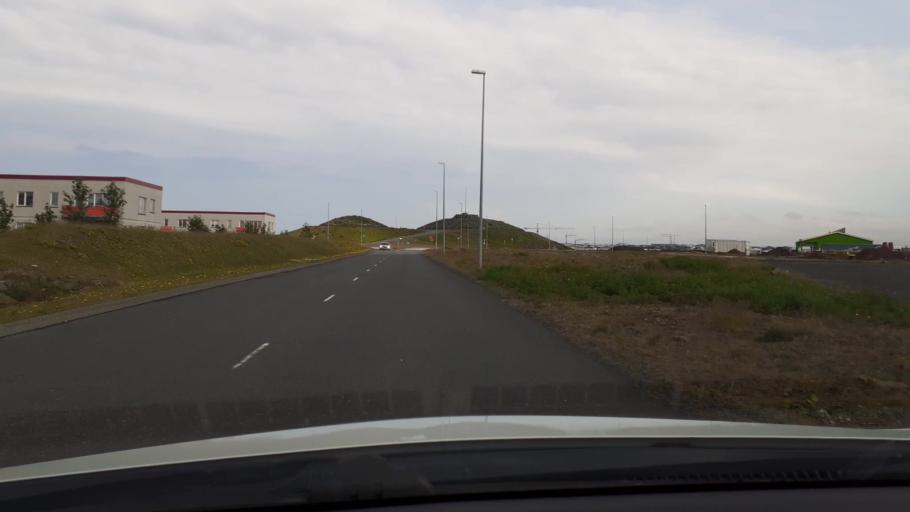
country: IS
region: Southern Peninsula
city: Reykjanesbaer
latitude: 63.9710
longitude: -22.5130
